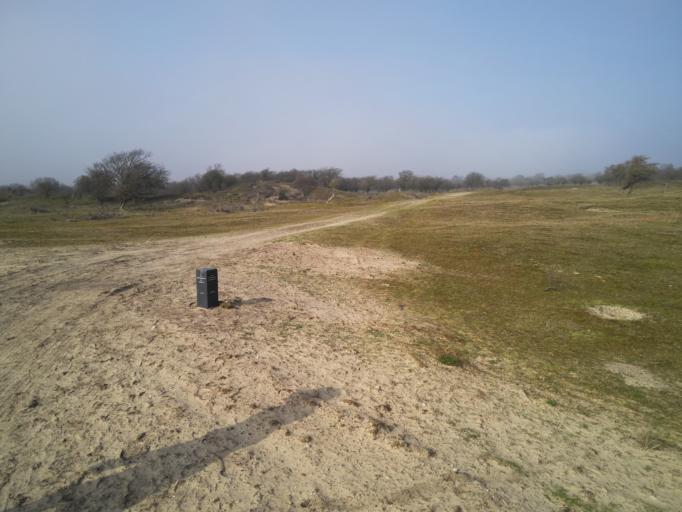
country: NL
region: South Holland
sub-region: Gemeente Hillegom
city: Hillegom
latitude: 52.3216
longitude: 4.5420
